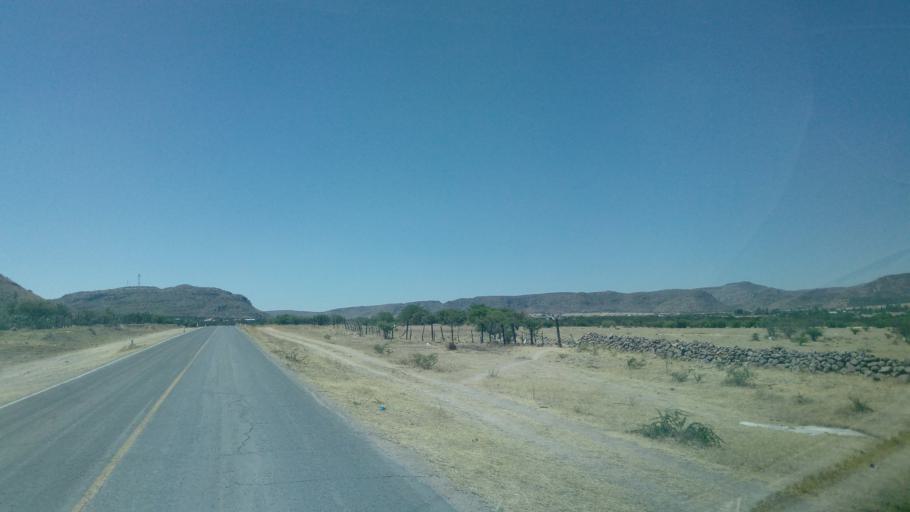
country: MX
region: Durango
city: Victoria de Durango
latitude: 24.1652
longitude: -104.7034
